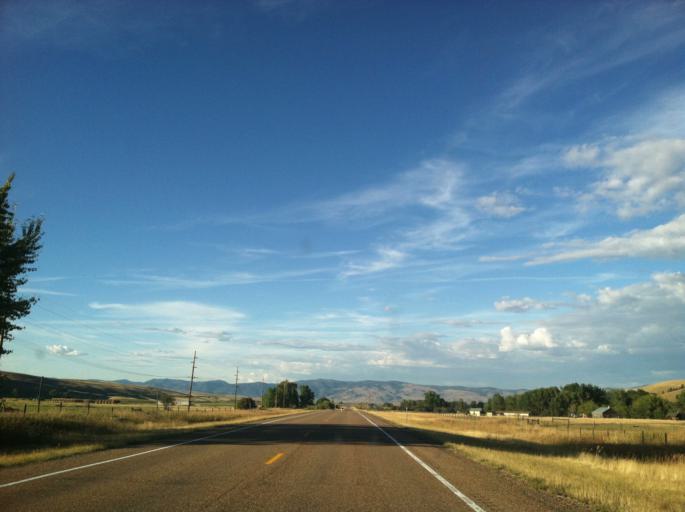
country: US
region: Montana
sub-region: Granite County
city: Philipsburg
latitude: 46.5346
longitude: -113.2223
